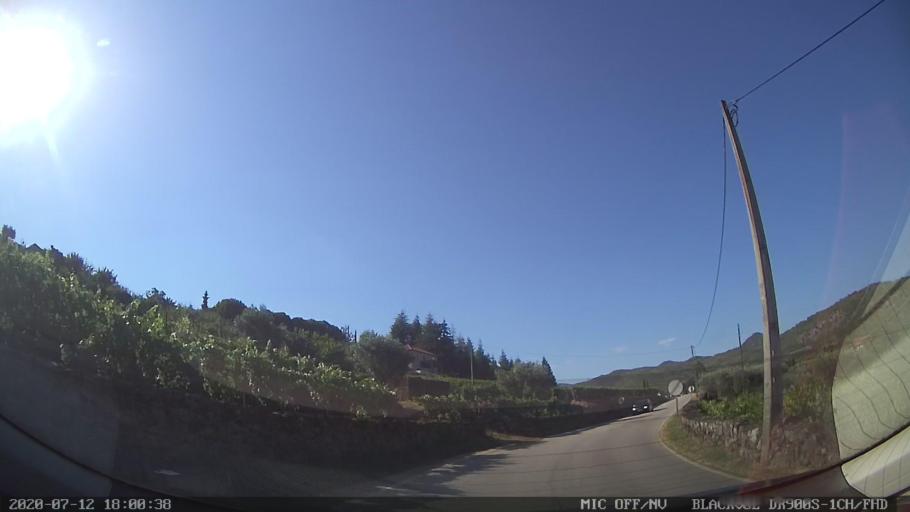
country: PT
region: Viseu
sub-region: Sao Joao da Pesqueira
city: Sao Joao da Pesqueira
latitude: 41.2568
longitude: -7.4409
